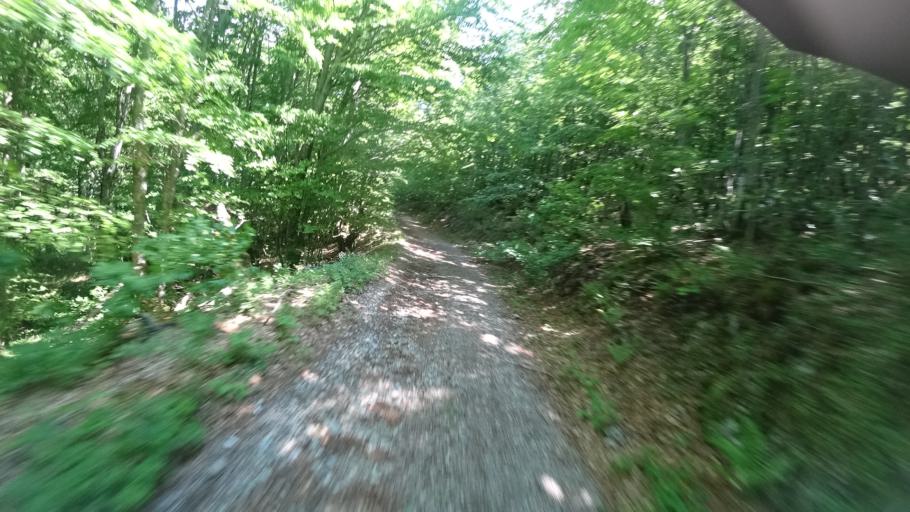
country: HR
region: Zadarska
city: Gracac
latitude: 44.4588
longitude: 15.9032
